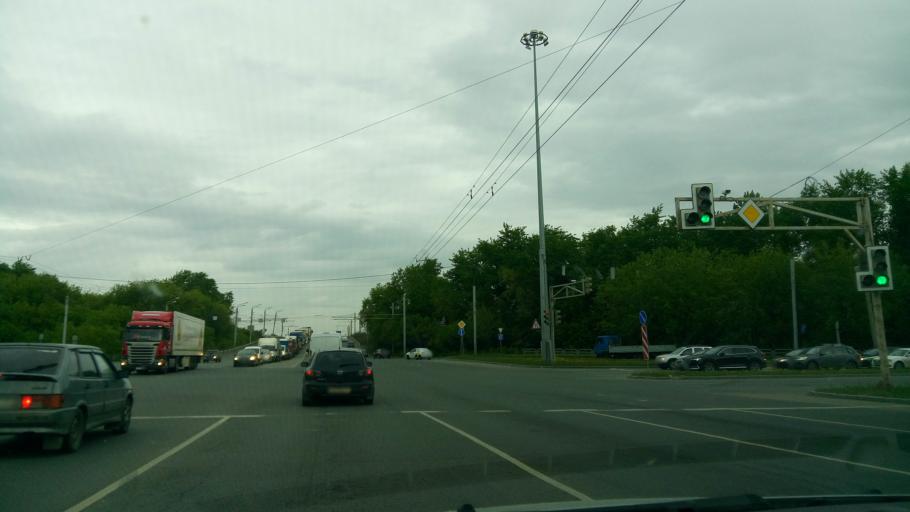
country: RU
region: Chelyabinsk
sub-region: Gorod Chelyabinsk
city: Chelyabinsk
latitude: 55.1943
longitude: 61.3862
